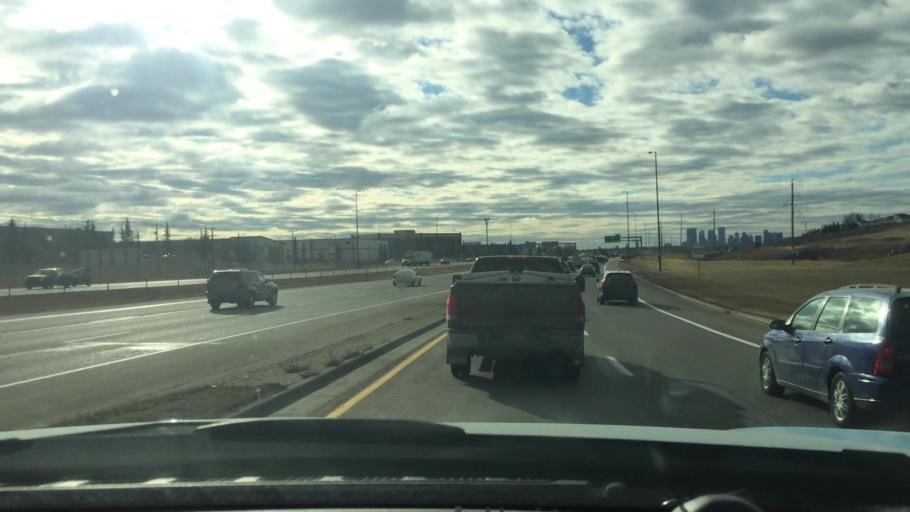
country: CA
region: Alberta
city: Calgary
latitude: 51.1235
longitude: -114.0463
